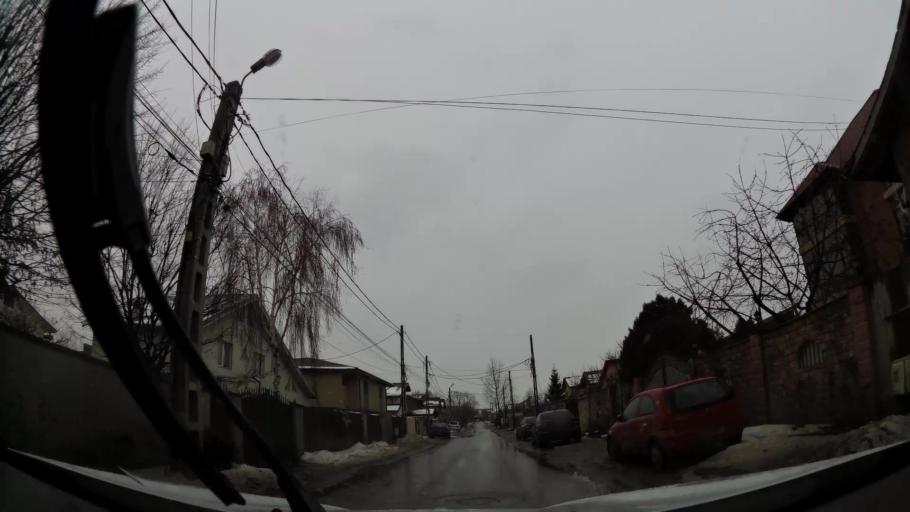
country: RO
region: Ilfov
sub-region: Comuna Bragadiru
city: Bragadiru
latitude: 44.3997
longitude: 26.0065
